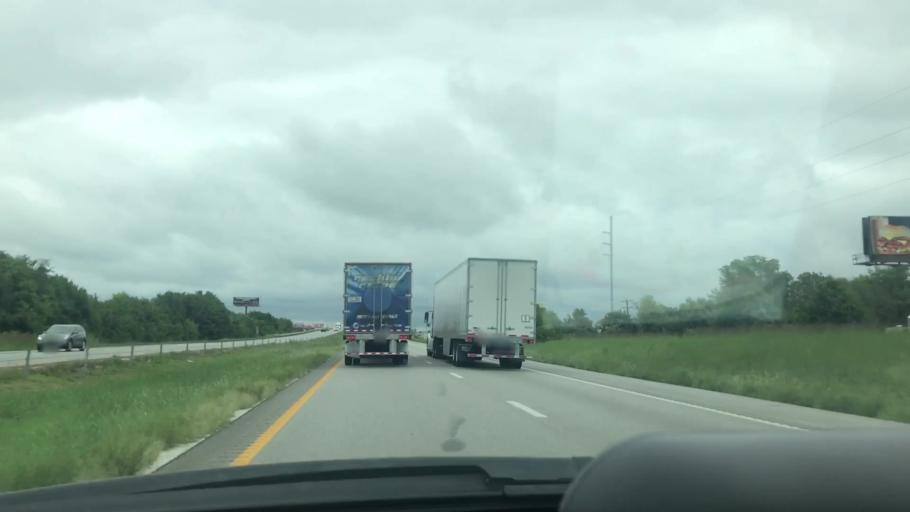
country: US
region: Missouri
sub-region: Greene County
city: Springfield
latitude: 37.2167
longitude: -93.3806
